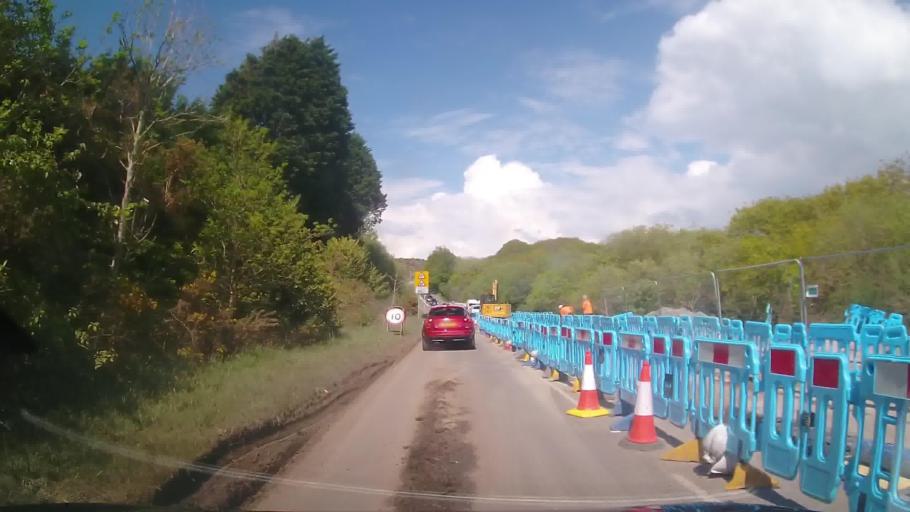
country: GB
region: Wales
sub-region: Gwynedd
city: Porthmadog
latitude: 52.9156
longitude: -4.1526
